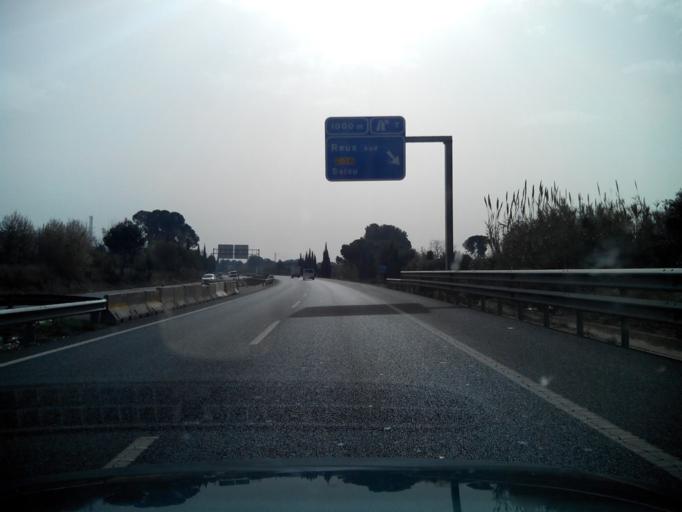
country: ES
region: Catalonia
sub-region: Provincia de Tarragona
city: Reus
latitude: 41.1341
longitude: 1.1033
